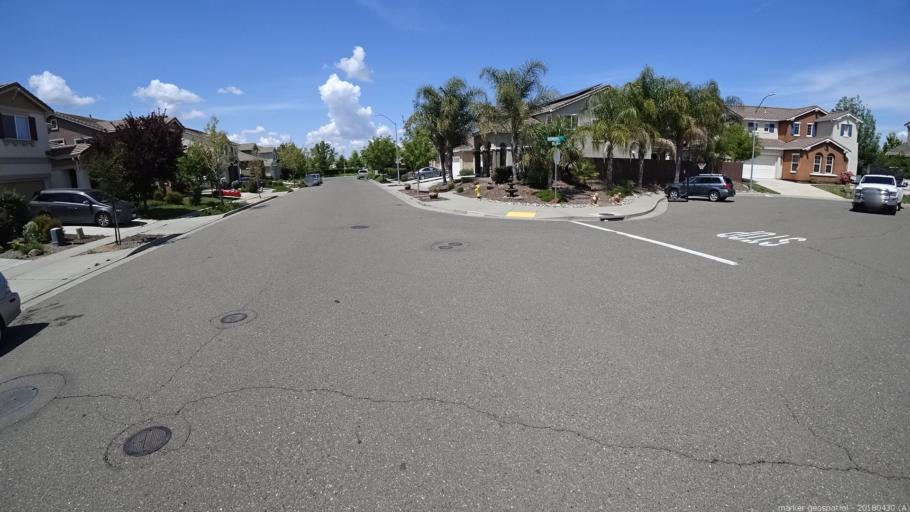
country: US
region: California
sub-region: Yolo County
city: West Sacramento
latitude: 38.5491
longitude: -121.5267
